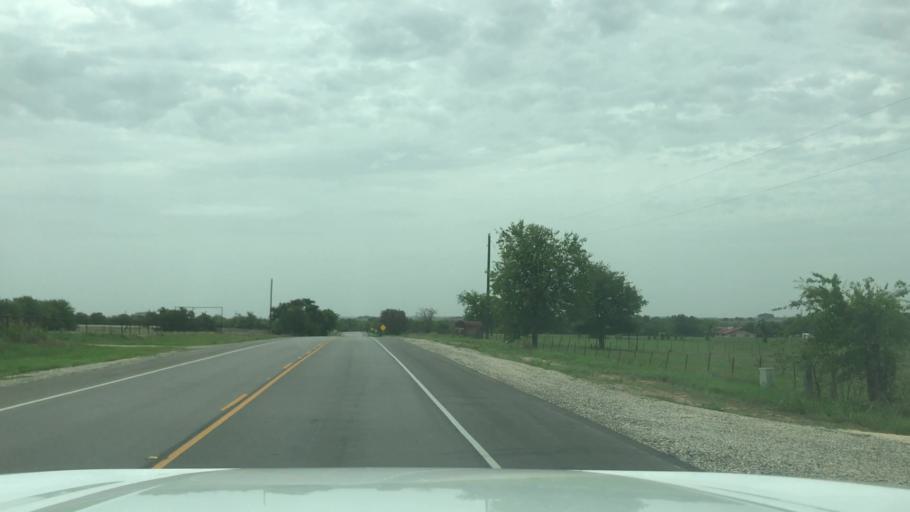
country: US
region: Texas
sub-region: Erath County
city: Dublin
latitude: 32.0644
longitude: -98.2152
